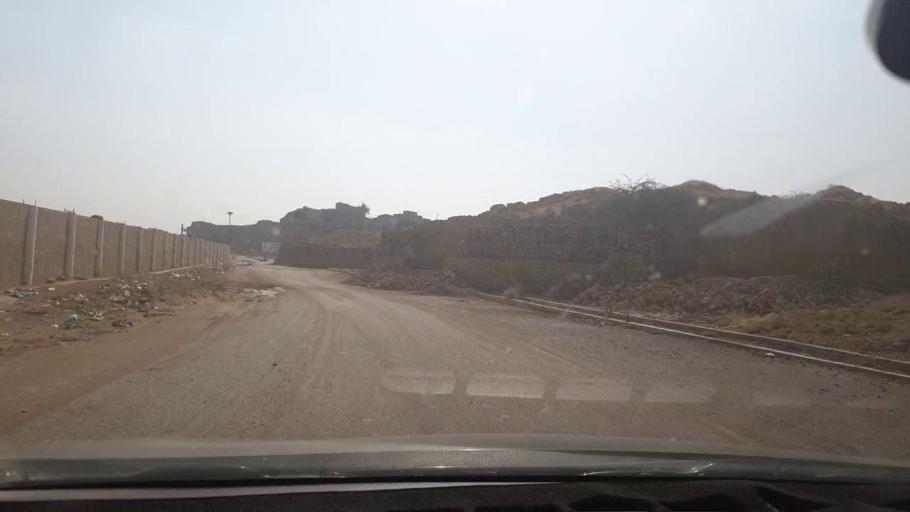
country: PK
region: Sindh
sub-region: Karachi District
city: Karachi
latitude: 24.9705
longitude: 66.9979
